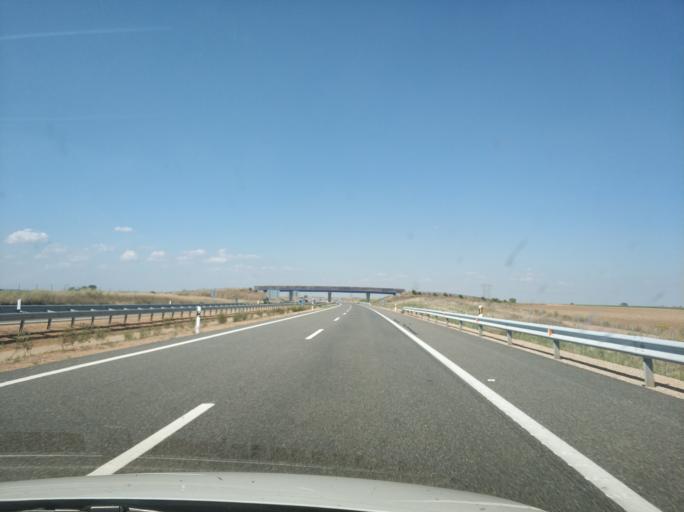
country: ES
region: Castille and Leon
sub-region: Provincia de Zamora
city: San Cebrian de Castro
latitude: 41.7286
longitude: -5.7738
